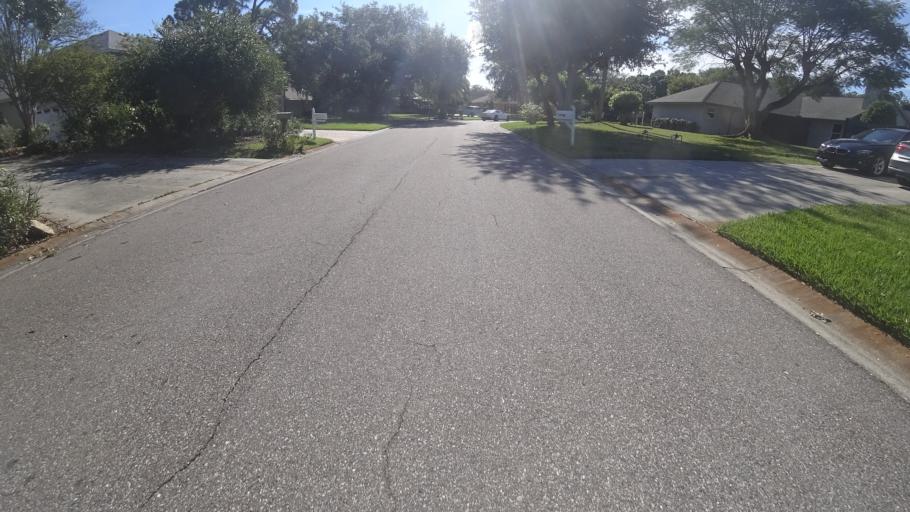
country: US
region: Florida
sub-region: Manatee County
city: West Bradenton
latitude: 27.5104
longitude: -82.6499
